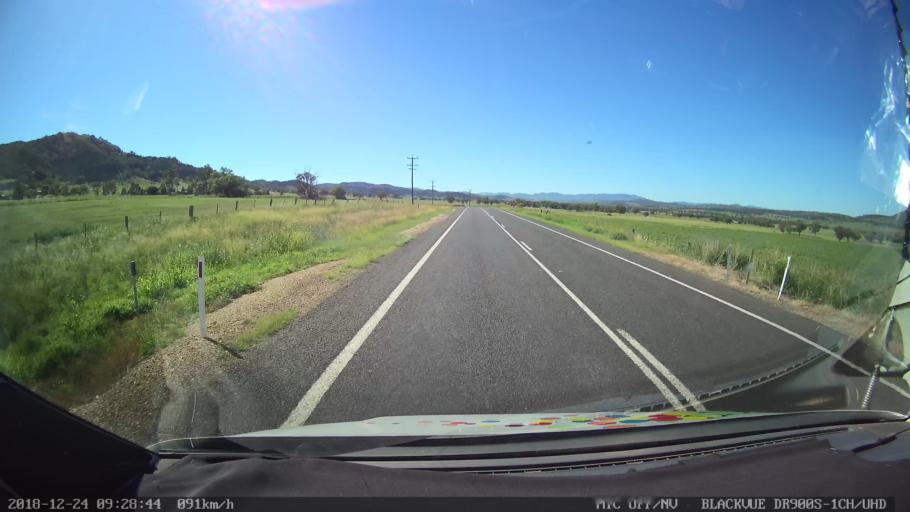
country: AU
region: New South Wales
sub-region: Liverpool Plains
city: Quirindi
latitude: -31.5413
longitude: 150.6913
